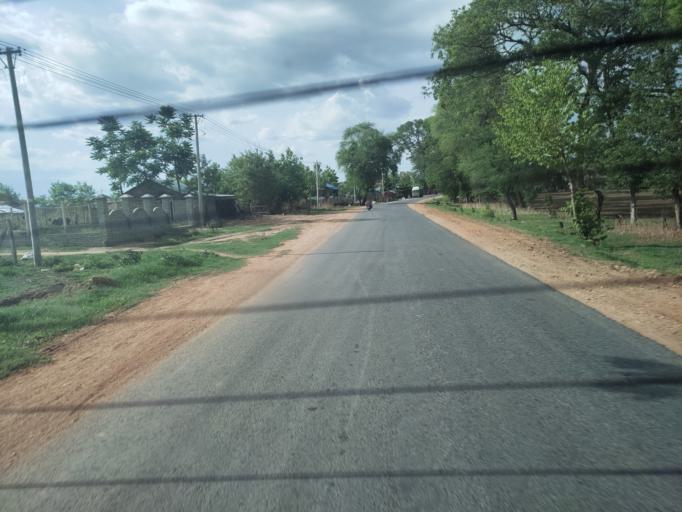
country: MM
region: Magway
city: Magway
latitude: 19.9922
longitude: 94.9882
